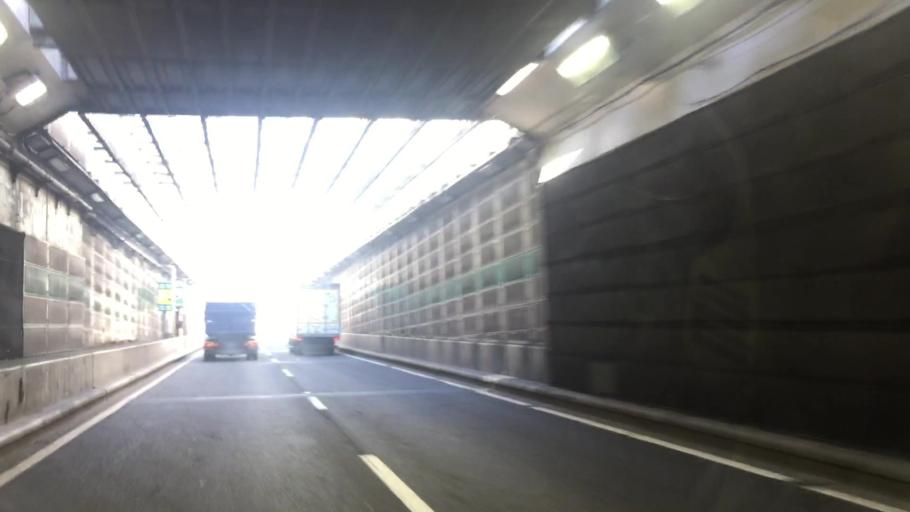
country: JP
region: Kanagawa
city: Yokohama
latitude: 35.4702
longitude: 139.6128
